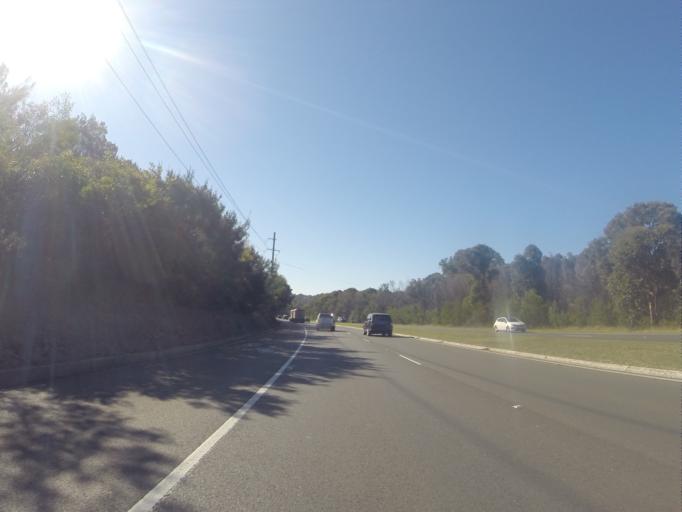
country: AU
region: New South Wales
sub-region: Sutherland Shire
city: Loftus
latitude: -34.0439
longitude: 151.0548
